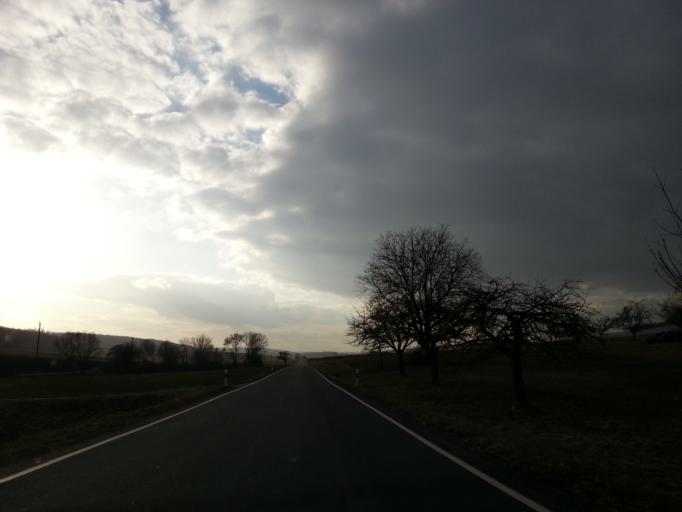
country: DE
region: Bavaria
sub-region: Regierungsbezirk Unterfranken
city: Helmstadt
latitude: 49.7623
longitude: 9.6980
